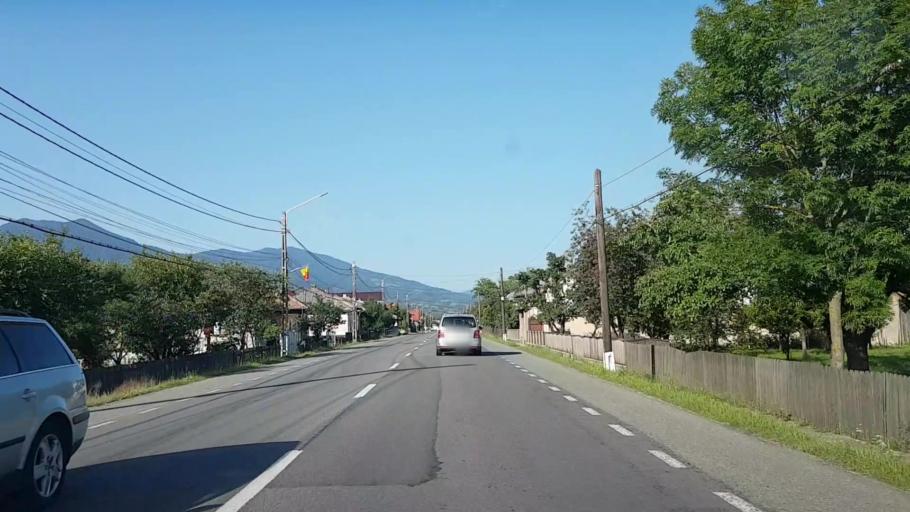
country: RO
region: Bistrita-Nasaud
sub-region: Comuna Josenii Bargaului
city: Josenii Bargaului
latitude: 47.2096
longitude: 24.6654
